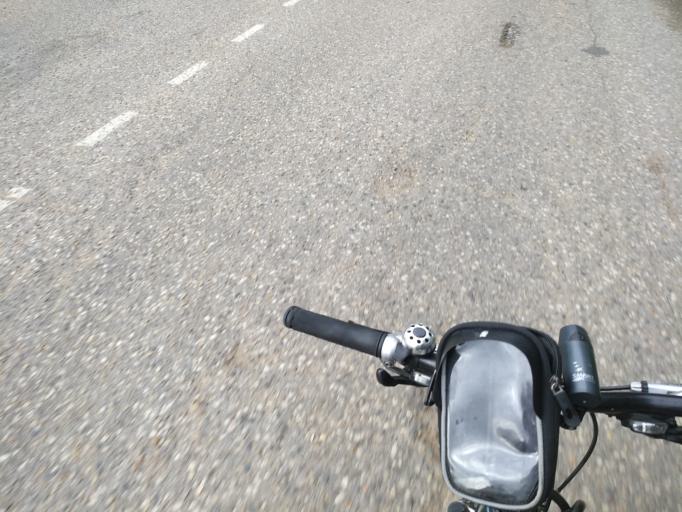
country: RU
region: Tverskaya
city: Krasnomayskiy
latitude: 57.6223
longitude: 34.4154
